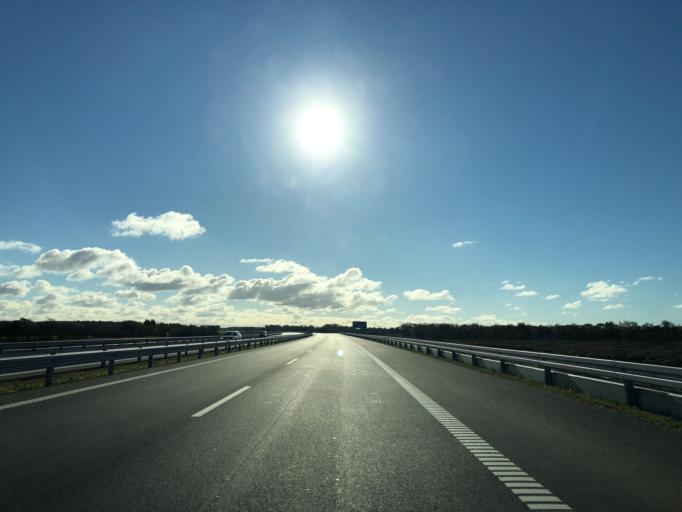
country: DK
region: Central Jutland
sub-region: Herning Kommune
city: Avlum
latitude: 56.3013
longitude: 8.7264
